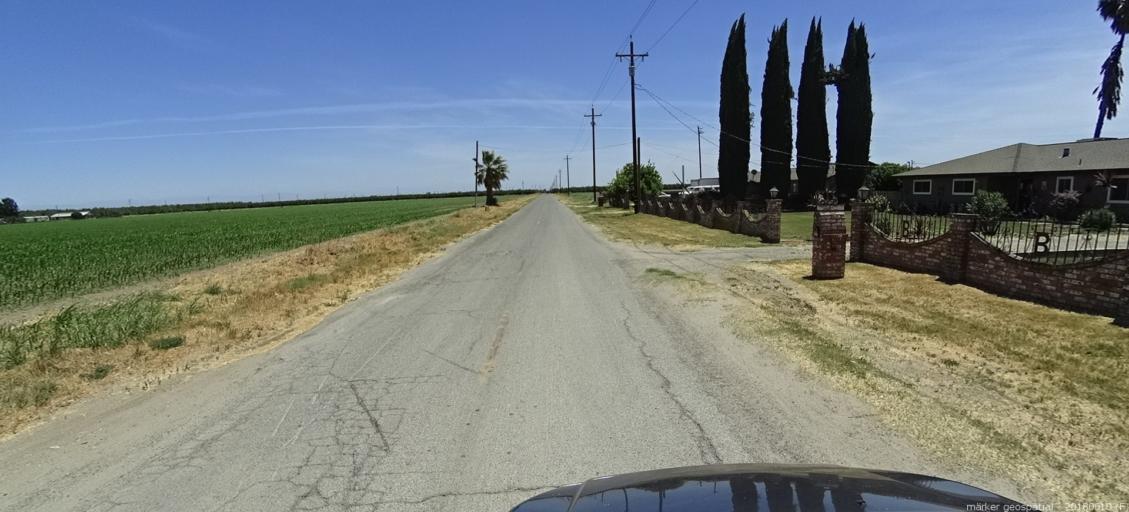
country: US
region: California
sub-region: Madera County
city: Chowchilla
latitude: 37.0544
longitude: -120.3422
